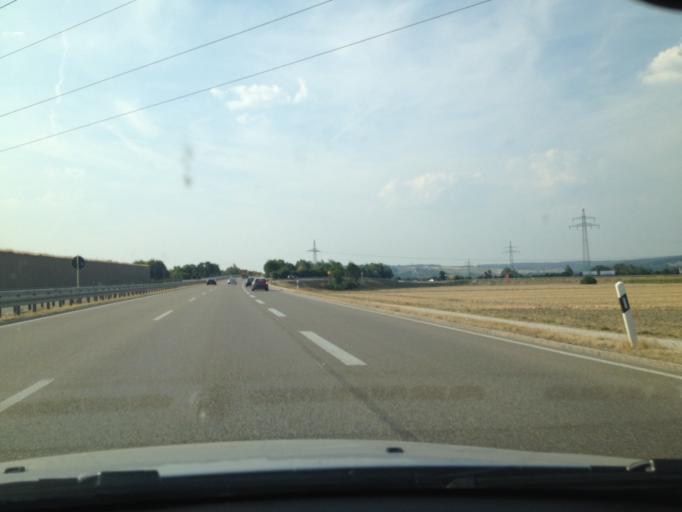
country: DE
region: Bavaria
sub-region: Swabia
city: Asbach-Baumenheim
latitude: 48.6889
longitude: 10.8162
